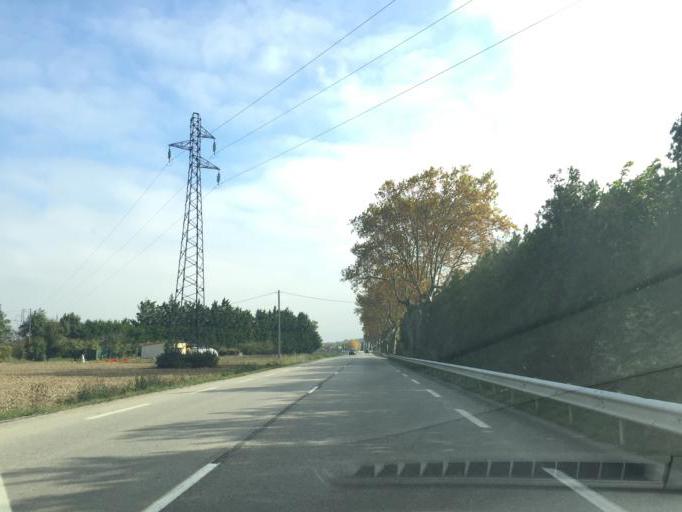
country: FR
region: Rhone-Alpes
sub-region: Departement de la Drome
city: Loriol-sur-Drome
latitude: 44.7549
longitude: 4.8052
